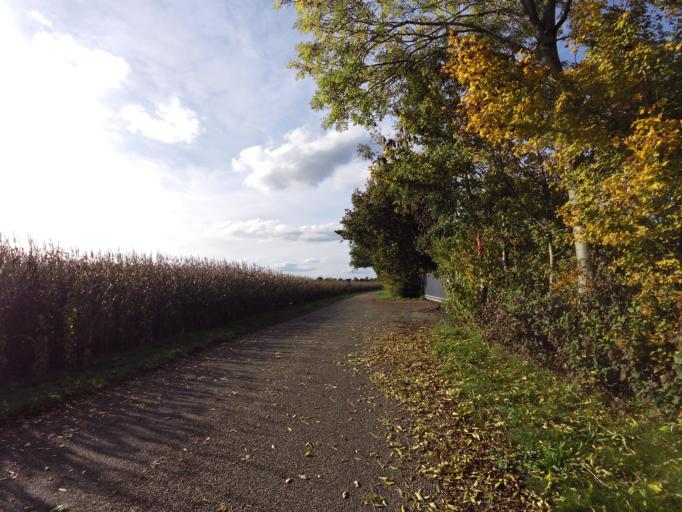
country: NL
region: Gelderland
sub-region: Gemeente Doetinchem
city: Doetinchem
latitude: 51.9677
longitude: 6.2116
